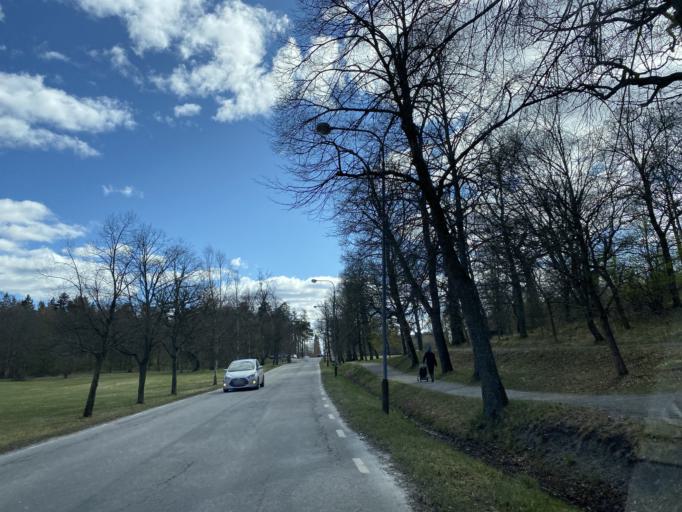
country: SE
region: Stockholm
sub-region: Nacka Kommun
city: Nacka
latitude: 59.3273
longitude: 18.1332
